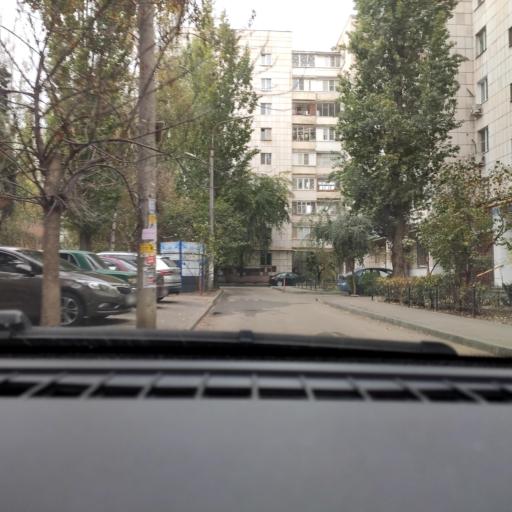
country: RU
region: Voronezj
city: Voronezh
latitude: 51.6686
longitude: 39.2453
